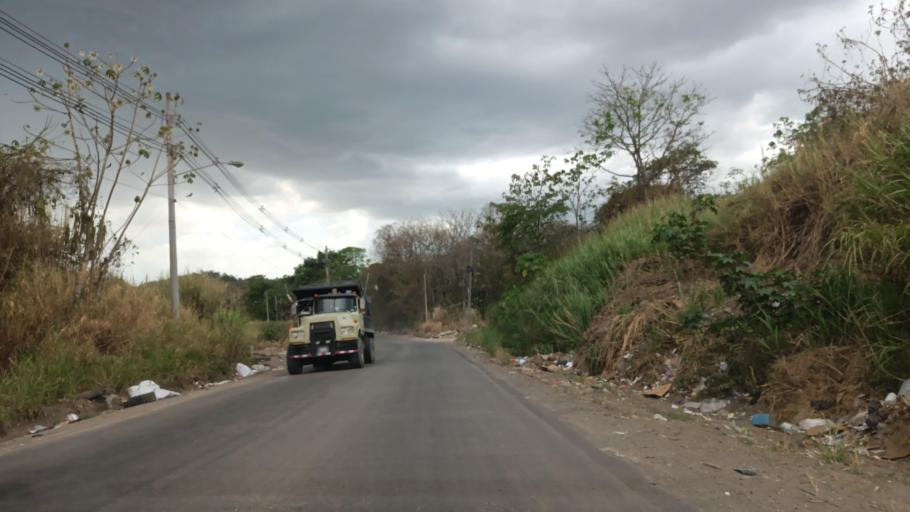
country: PA
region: Panama
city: Las Cumbres
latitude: 9.0504
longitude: -79.5635
